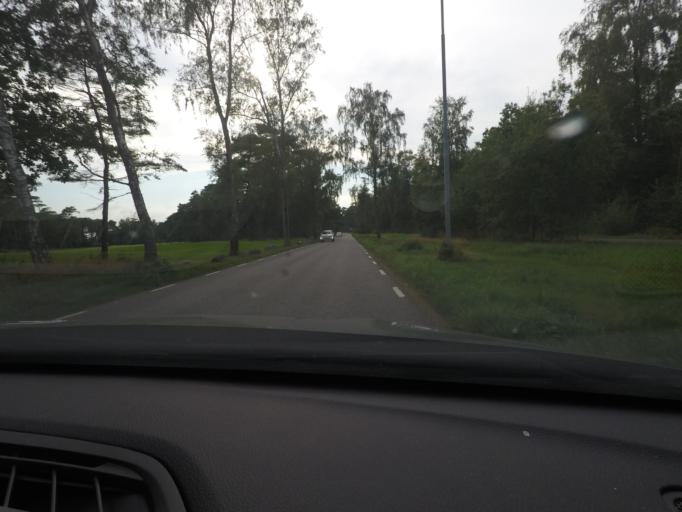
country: SE
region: Halland
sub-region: Halmstads Kommun
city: Frosakull
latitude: 56.6549
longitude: 12.7490
